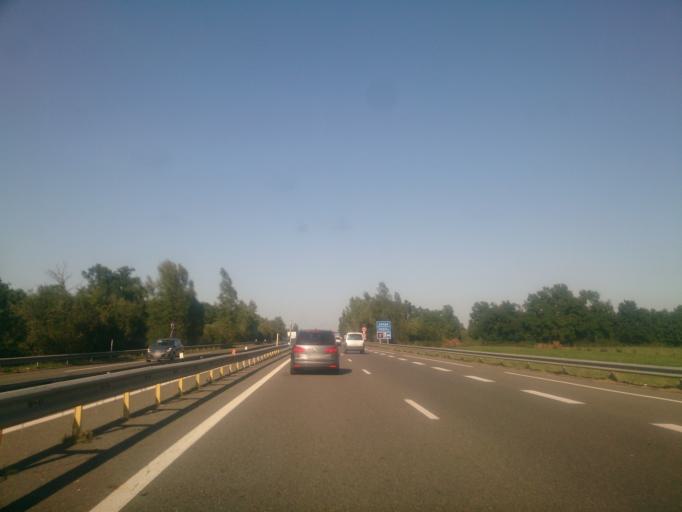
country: FR
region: Midi-Pyrenees
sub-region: Departement du Tarn-et-Garonne
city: Montauban
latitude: 44.0474
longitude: 1.3979
